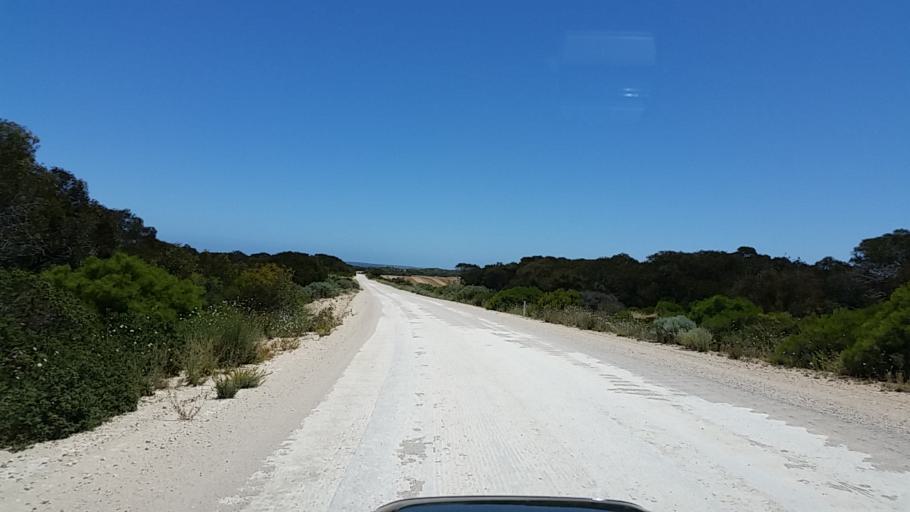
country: AU
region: South Australia
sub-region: Yorke Peninsula
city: Honiton
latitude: -35.2188
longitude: 137.0838
